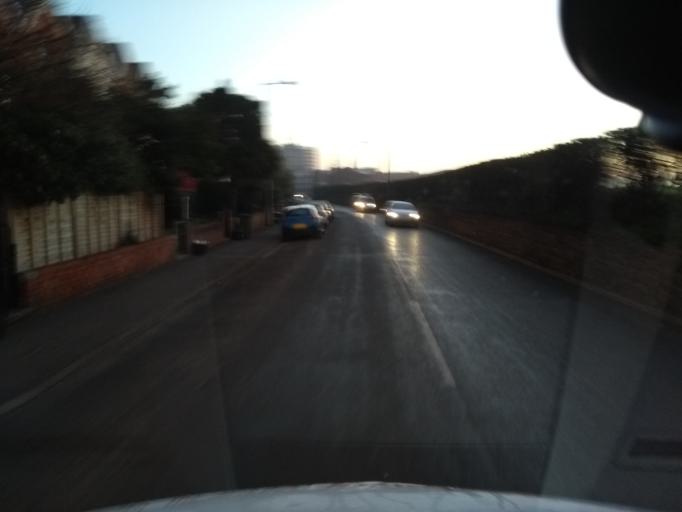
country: GB
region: England
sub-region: Somerset
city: Bridgwater
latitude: 51.1242
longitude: -3.0145
